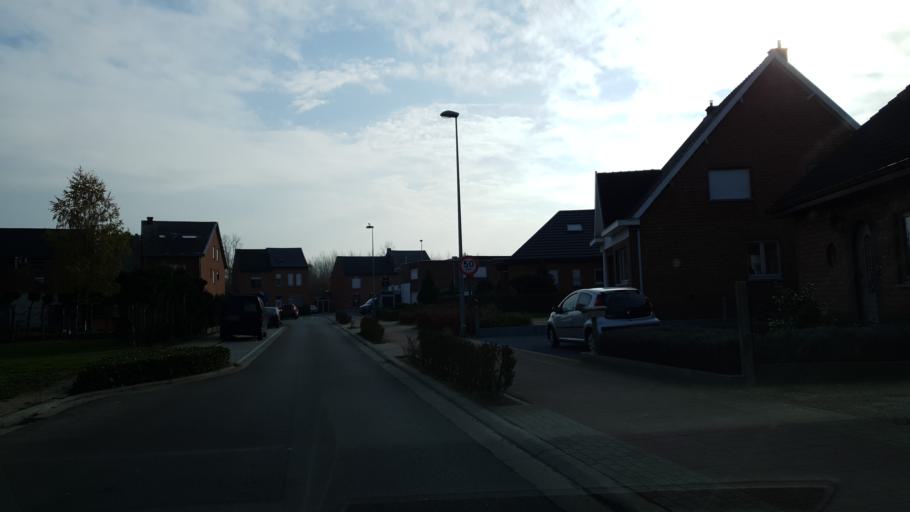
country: BE
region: Flanders
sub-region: Provincie Vlaams-Brabant
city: Boortmeerbeek
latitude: 50.9867
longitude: 4.5744
